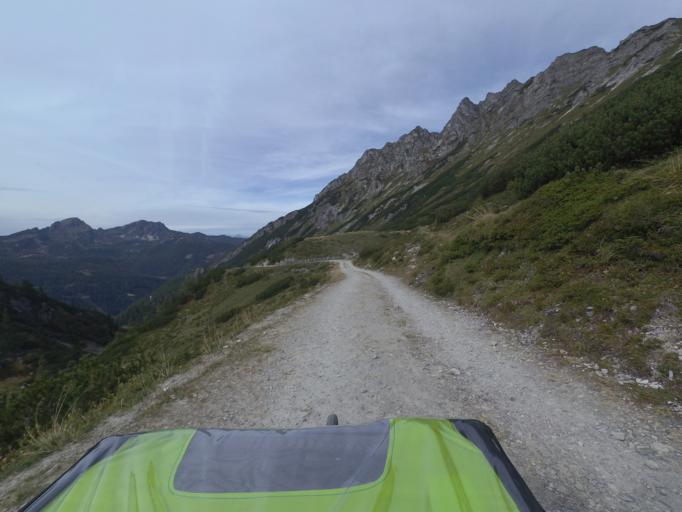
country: AT
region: Salzburg
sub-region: Politischer Bezirk Sankt Johann im Pongau
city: Untertauern
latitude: 47.2855
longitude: 13.5998
